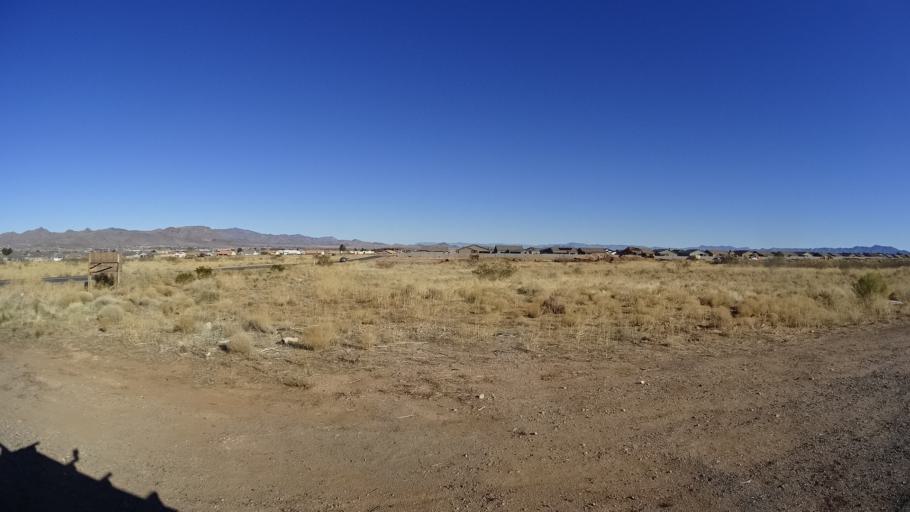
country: US
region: Arizona
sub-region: Mohave County
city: Kingman
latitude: 35.1885
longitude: -114.0022
